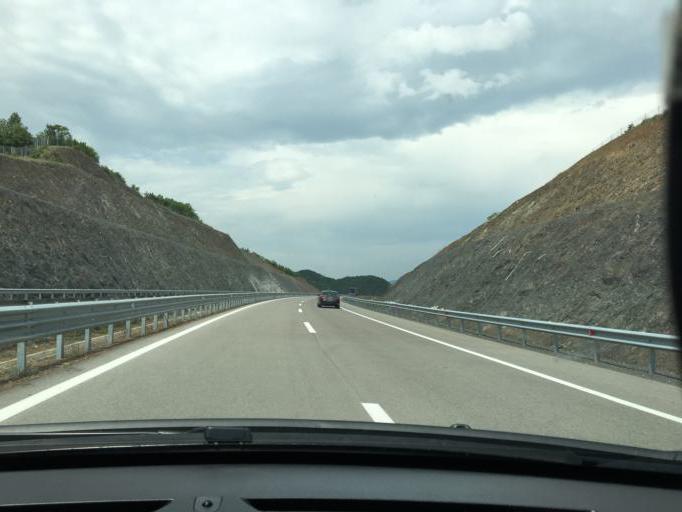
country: MK
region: Gevgelija
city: Miravci
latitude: 41.3370
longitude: 22.3830
